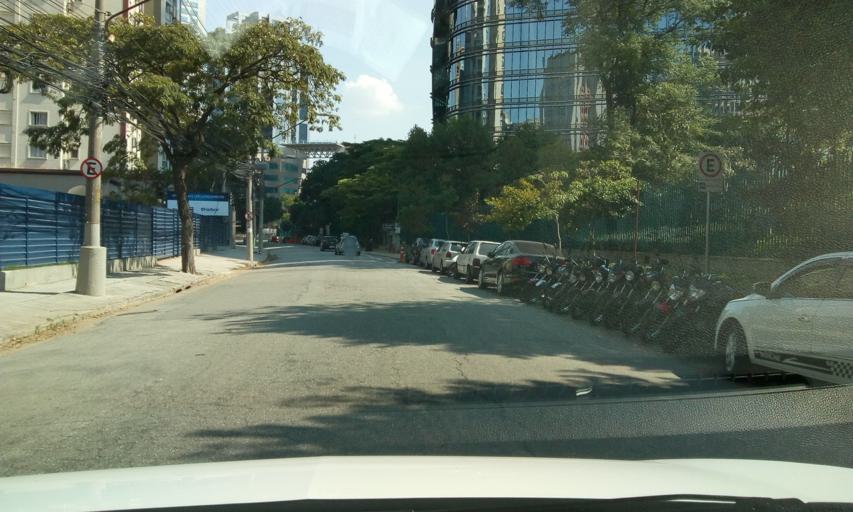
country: BR
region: Sao Paulo
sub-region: Sao Paulo
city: Sao Paulo
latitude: -23.5925
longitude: -46.6870
